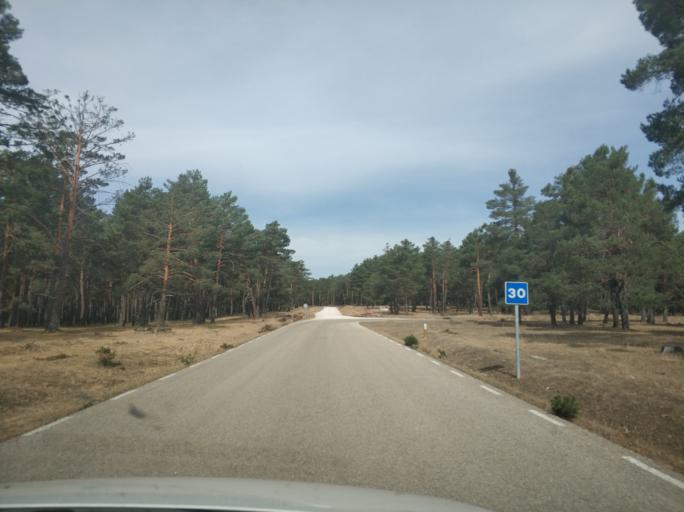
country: ES
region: Castille and Leon
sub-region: Provincia de Soria
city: Navaleno
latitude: 41.8673
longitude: -2.9446
